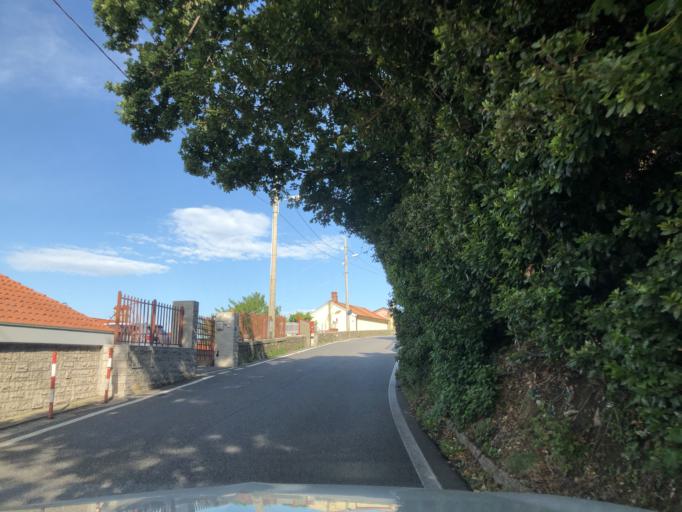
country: IT
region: Friuli Venezia Giulia
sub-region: Provincia di Trieste
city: Prosecco-Contovello
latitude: 45.6858
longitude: 13.7547
